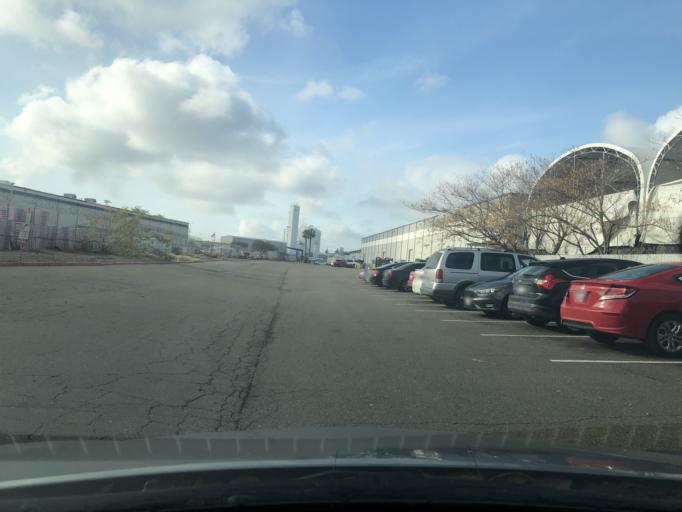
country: US
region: California
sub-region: Sacramento County
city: Rosemont
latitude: 38.5210
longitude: -121.3769
